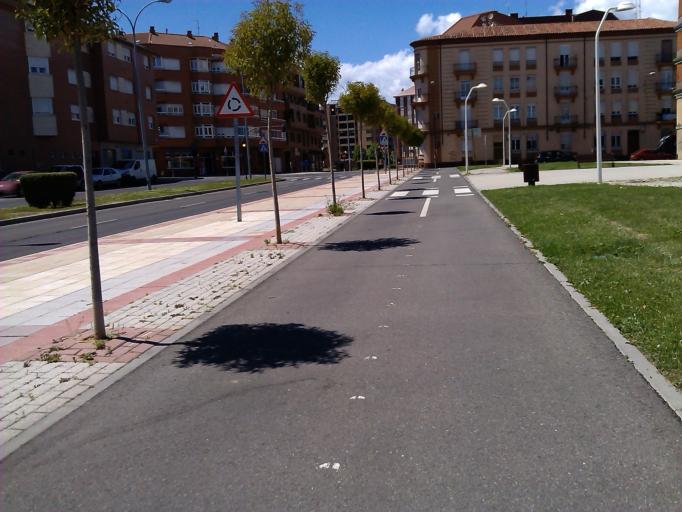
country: ES
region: Castille and Leon
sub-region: Provincia de Leon
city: Leon
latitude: 42.6030
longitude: -5.5590
